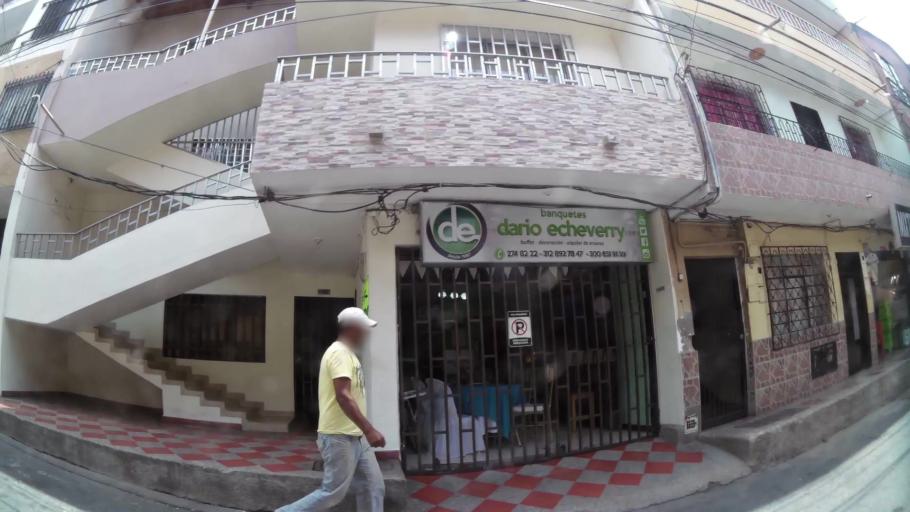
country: CO
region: Antioquia
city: Municipio de Copacabana
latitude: 6.3469
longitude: -75.5056
